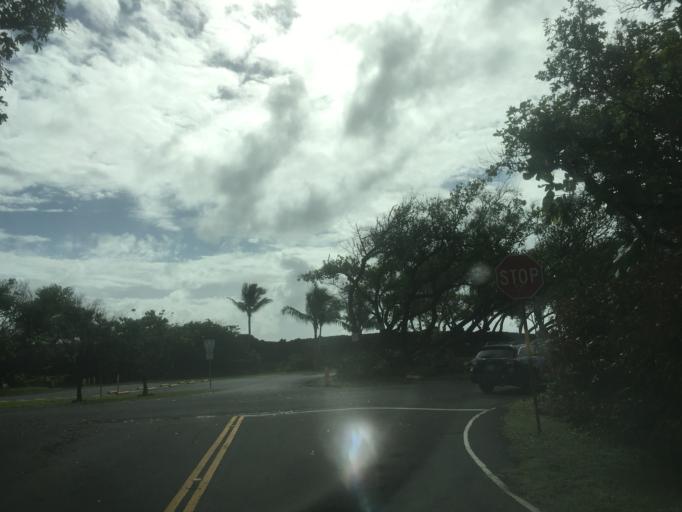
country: US
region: Hawaii
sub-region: Hawaii County
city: Leilani Estates
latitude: 19.4583
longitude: -154.8420
